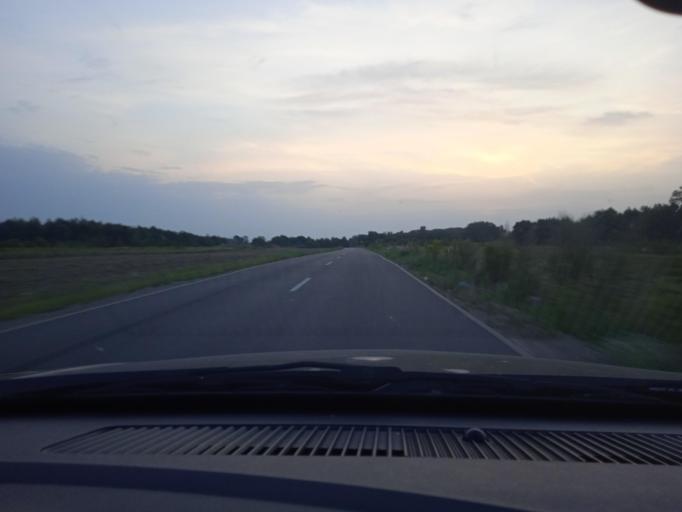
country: PL
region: Masovian Voivodeship
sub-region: Powiat nowodworski
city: Pomiechowek
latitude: 52.4646
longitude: 20.7066
